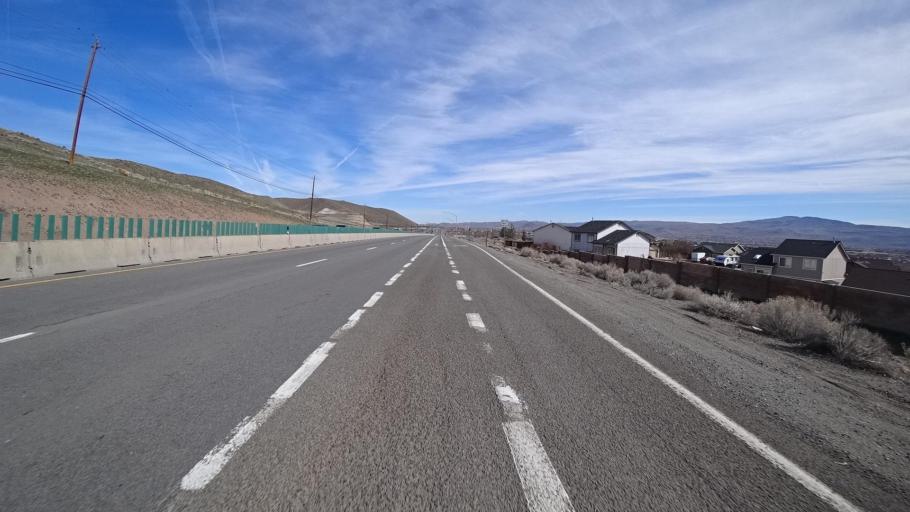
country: US
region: Nevada
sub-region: Washoe County
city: Sun Valley
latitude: 39.6015
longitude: -119.7352
